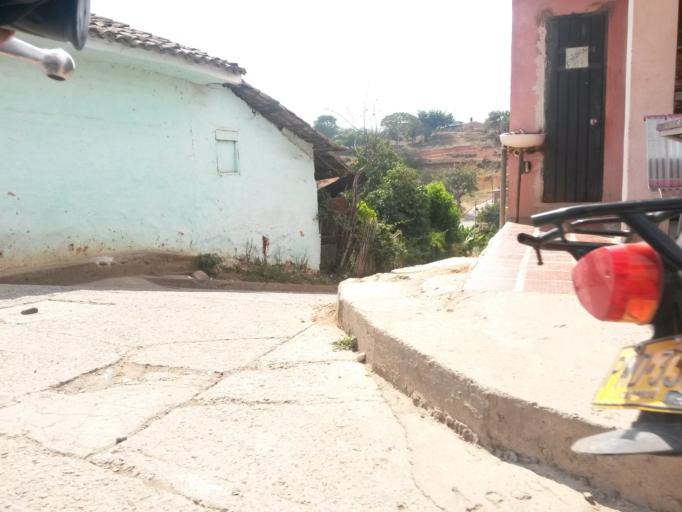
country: CO
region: Cauca
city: Buenos Aires
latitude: 3.0161
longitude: -76.6424
